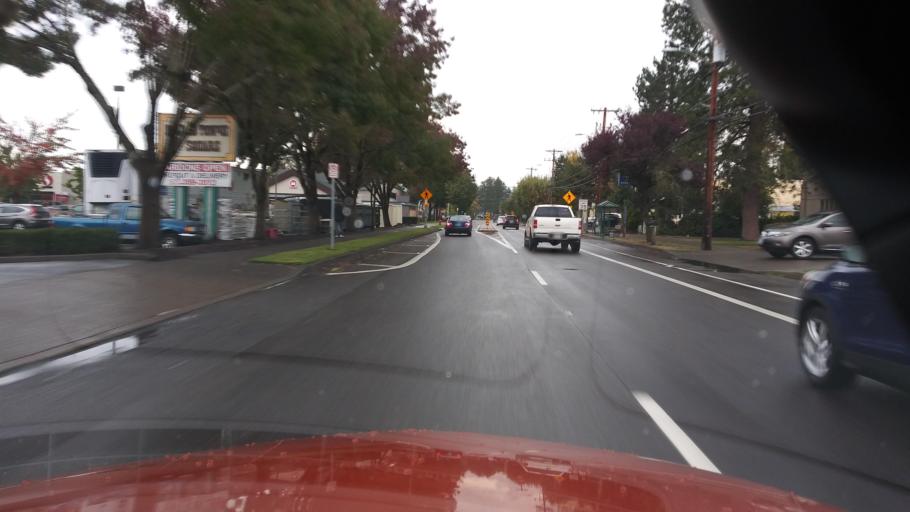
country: US
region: Oregon
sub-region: Washington County
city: Forest Grove
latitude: 45.5202
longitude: -123.0937
